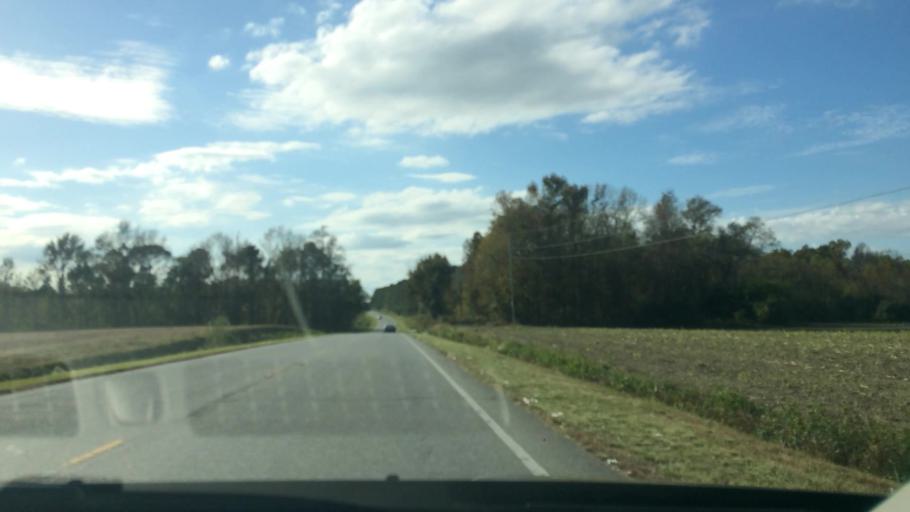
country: US
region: North Carolina
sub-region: Greene County
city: Snow Hill
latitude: 35.4419
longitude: -77.8144
